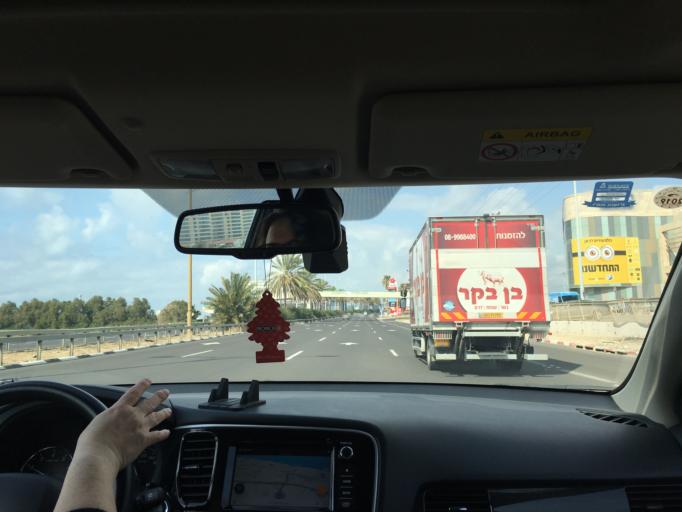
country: IL
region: Tel Aviv
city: Herzliya Pituah
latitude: 32.1456
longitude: 34.8031
